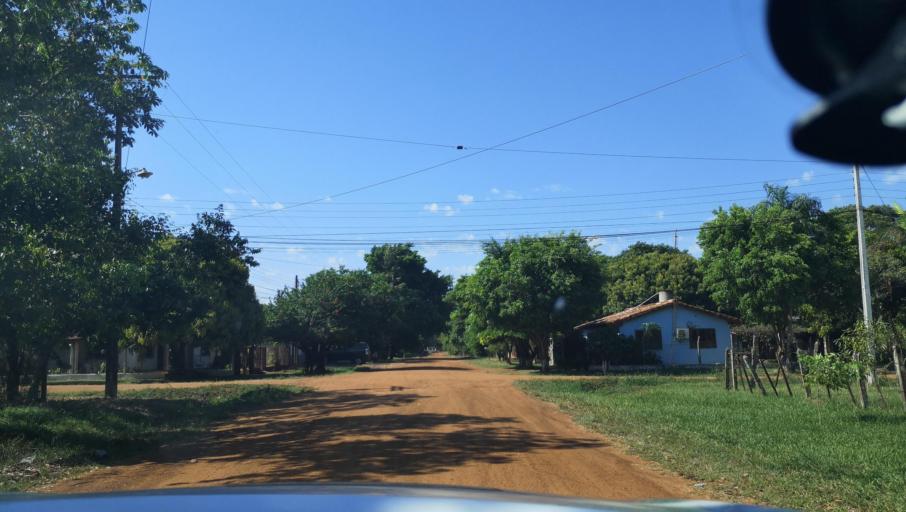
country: PY
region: Itapua
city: Carmen del Parana
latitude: -27.1671
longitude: -56.2348
